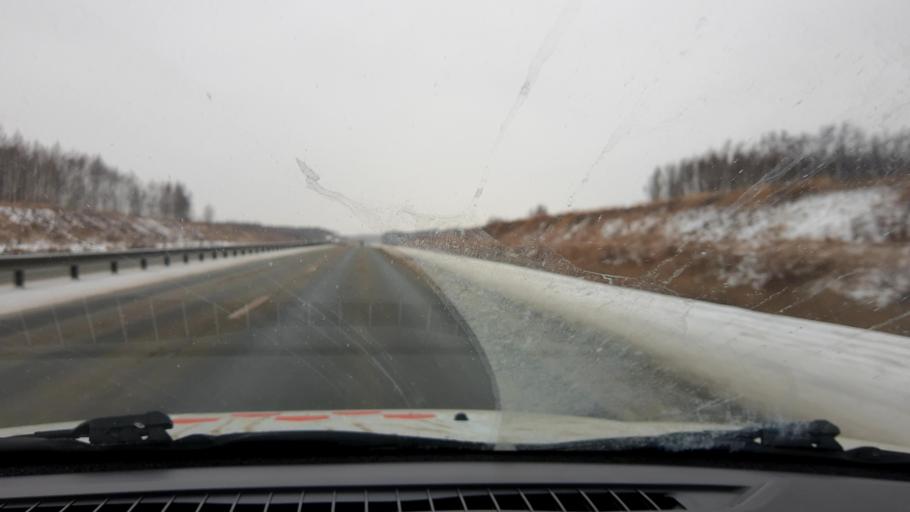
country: RU
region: Nizjnij Novgorod
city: Afonino
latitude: 56.1045
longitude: 44.0042
